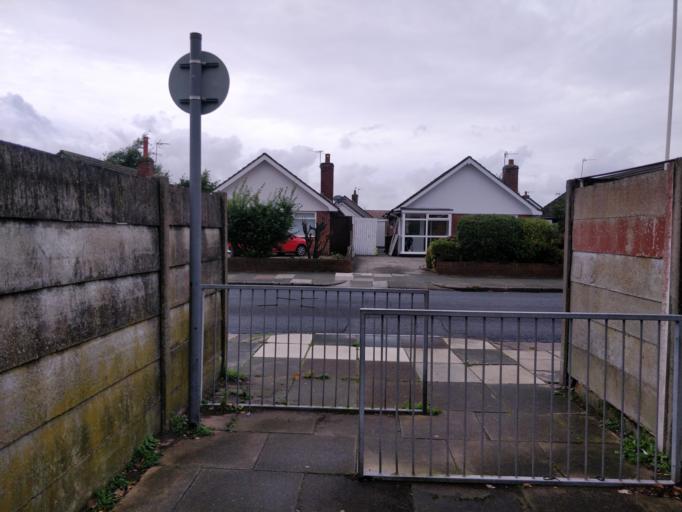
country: GB
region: England
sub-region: Sefton
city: Southport
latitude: 53.6707
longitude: -2.9673
